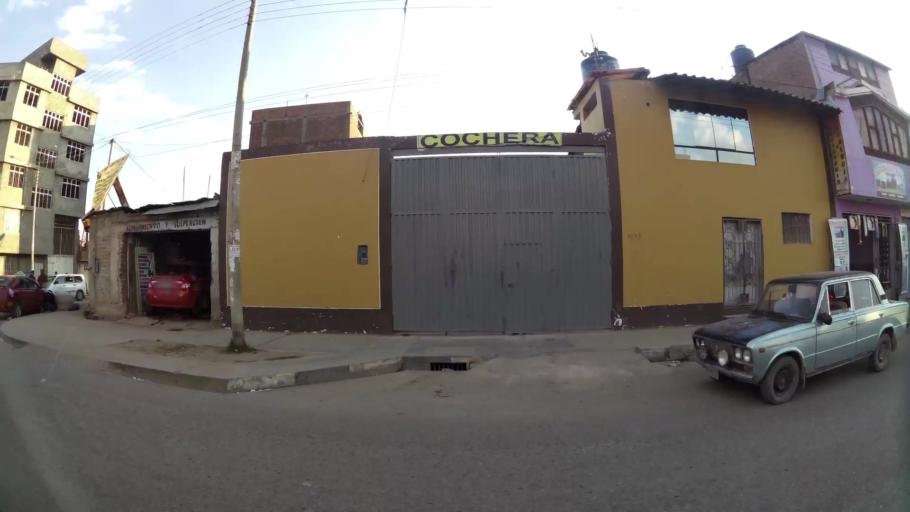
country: PE
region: Junin
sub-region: Provincia de Huancayo
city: El Tambo
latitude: -12.0497
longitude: -75.2156
